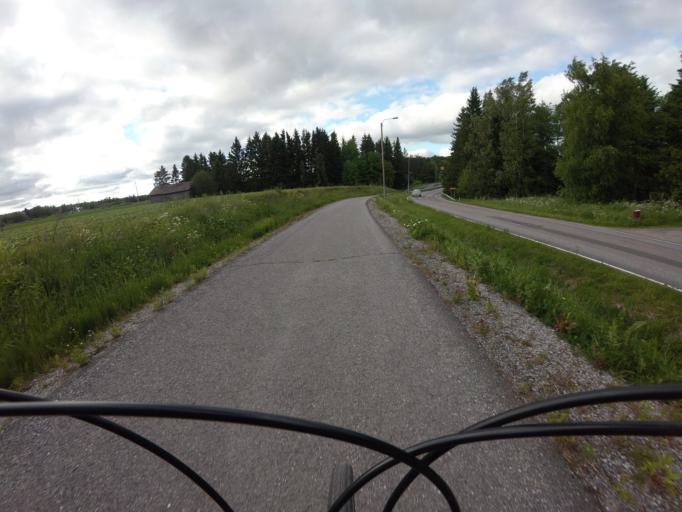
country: FI
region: Varsinais-Suomi
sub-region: Turku
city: Vahto
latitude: 60.5344
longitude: 22.3438
